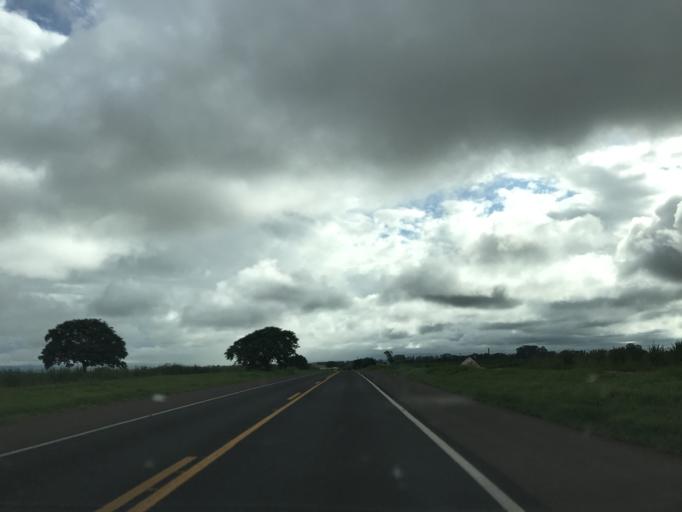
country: BR
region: Sao Paulo
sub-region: Penapolis
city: Penapolis
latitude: -21.4868
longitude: -50.2164
